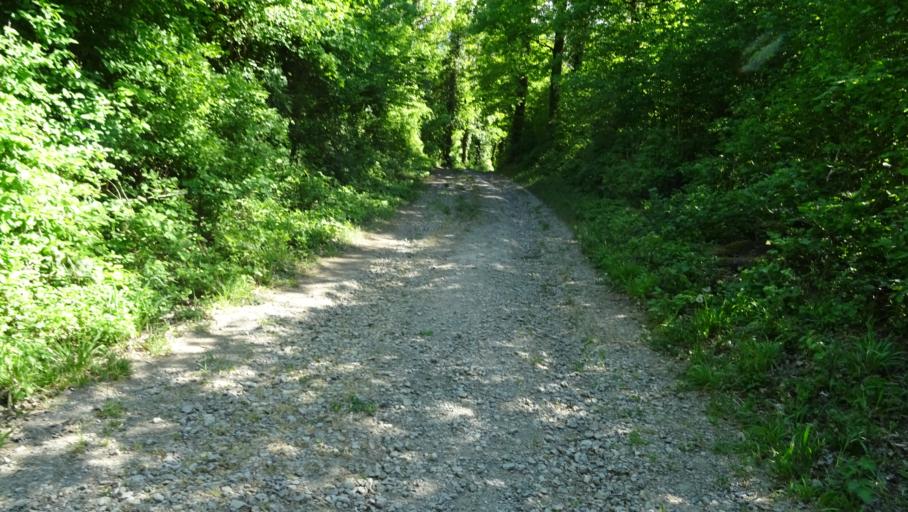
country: DE
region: Baden-Wuerttemberg
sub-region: Karlsruhe Region
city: Neckarzimmern
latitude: 49.3227
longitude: 9.1298
